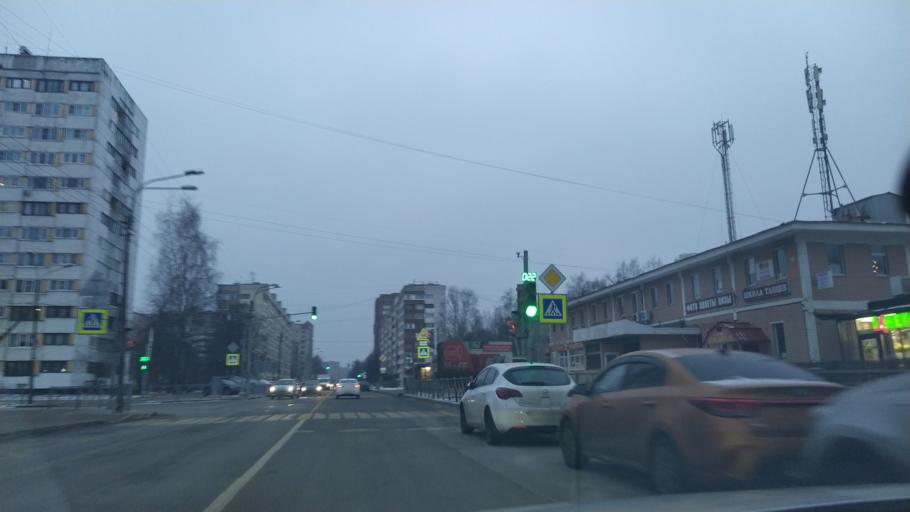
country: RU
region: St.-Petersburg
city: Grazhdanka
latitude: 60.0427
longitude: 30.4103
